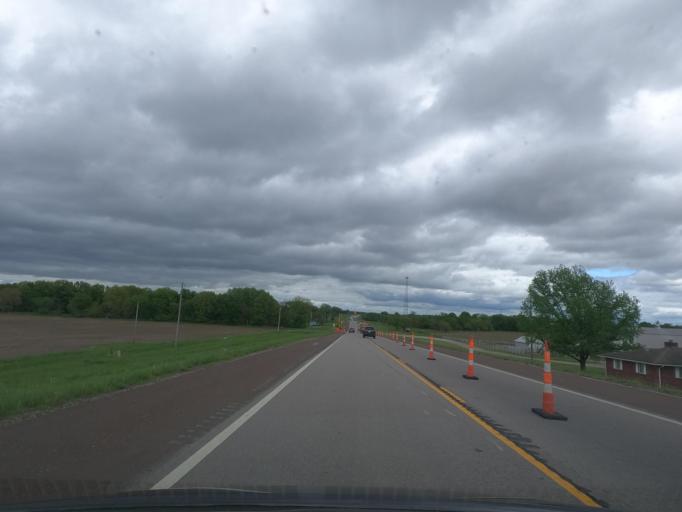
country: US
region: Kansas
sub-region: Crawford County
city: Pittsburg
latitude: 37.3384
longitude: -94.6448
